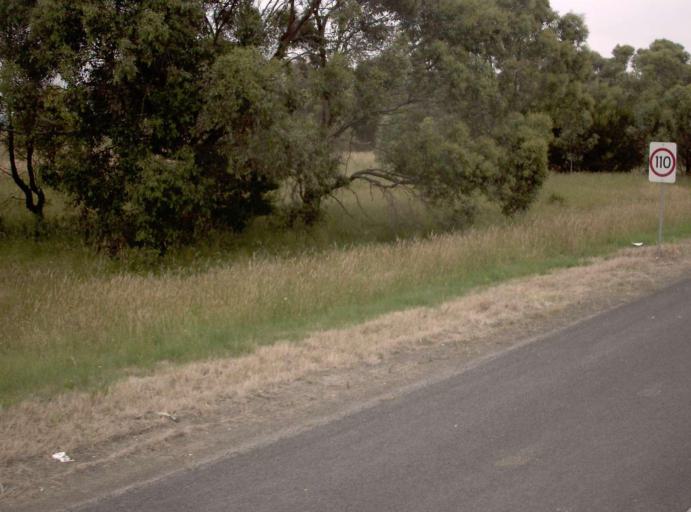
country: AU
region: Victoria
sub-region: Latrobe
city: Morwell
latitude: -38.2341
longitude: 146.4545
